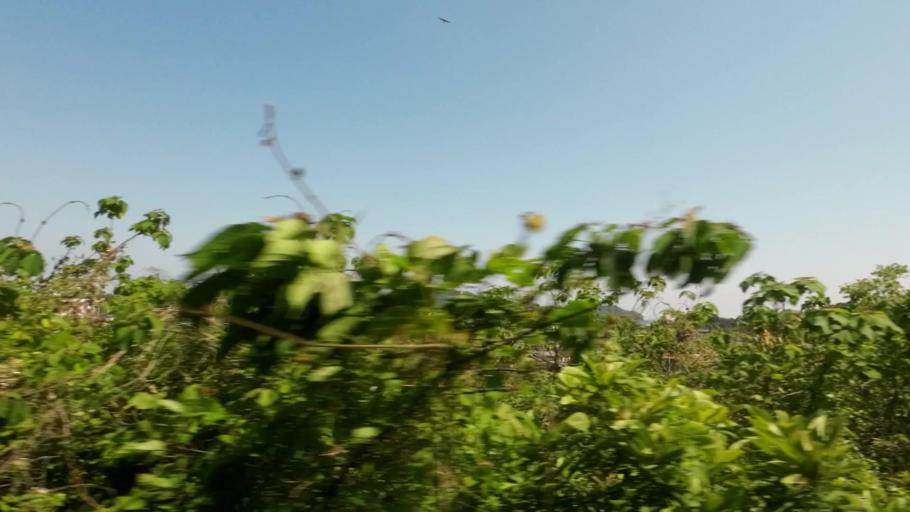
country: JP
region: Ehime
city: Niihama
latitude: 33.9721
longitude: 133.3536
